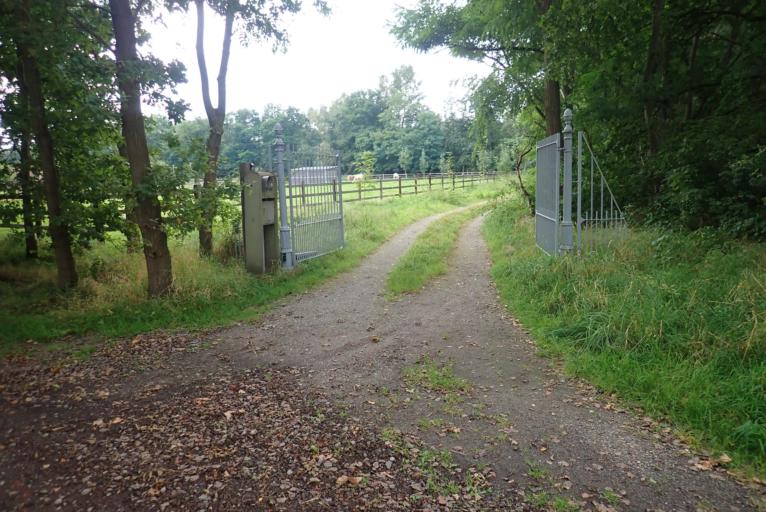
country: BE
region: Flanders
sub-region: Provincie Vlaams-Brabant
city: Tremelo
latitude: 51.0299
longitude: 4.6776
